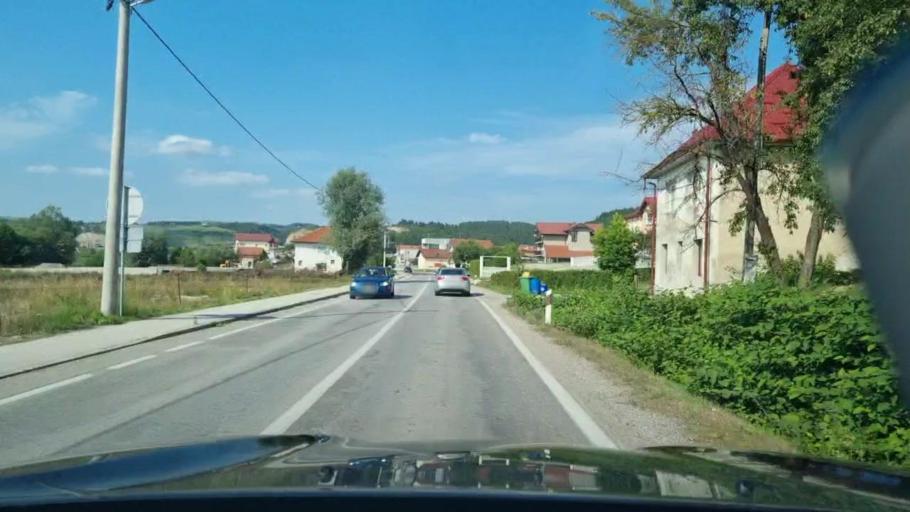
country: BA
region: Federation of Bosnia and Herzegovina
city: Coralici
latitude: 44.9831
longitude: 15.8926
